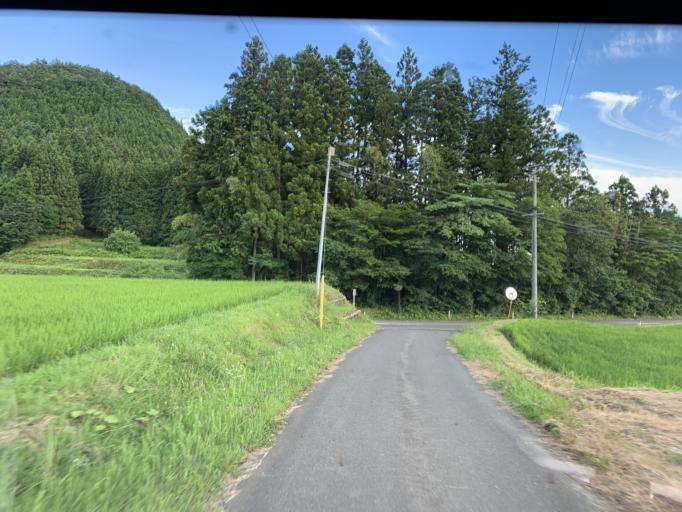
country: JP
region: Iwate
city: Ichinoseki
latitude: 38.8918
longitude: 140.9513
